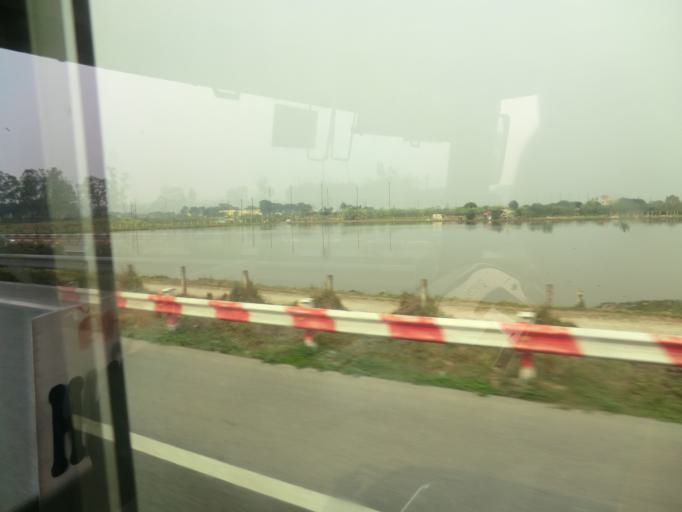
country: VN
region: Ha Noi
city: Thuong Tin
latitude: 20.8545
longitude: 105.8827
